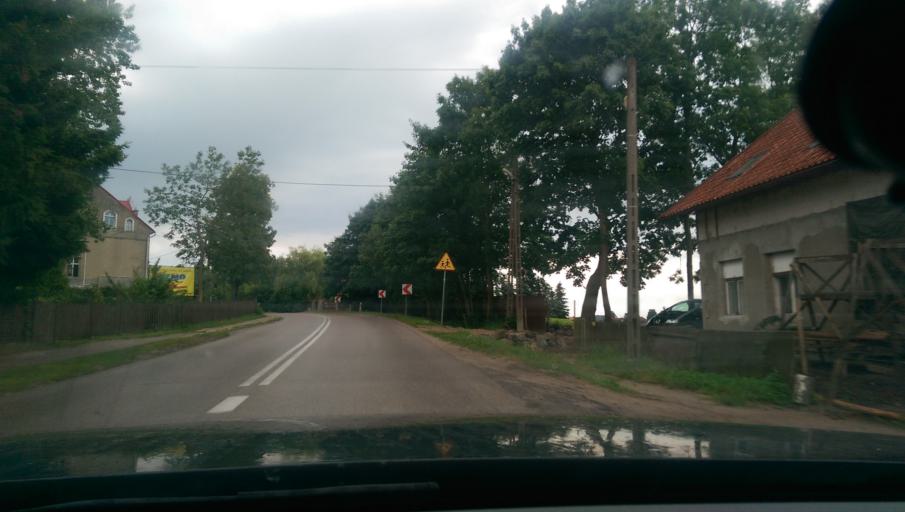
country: PL
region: Warmian-Masurian Voivodeship
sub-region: Powiat piski
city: Ruciane-Nida
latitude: 53.6878
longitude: 21.4919
